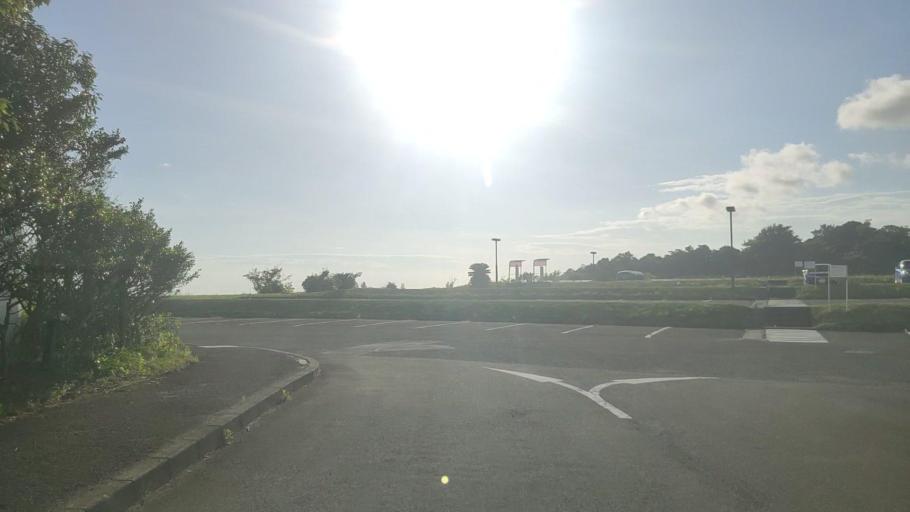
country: JP
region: Wakayama
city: Tanabe
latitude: 33.7686
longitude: 135.3014
